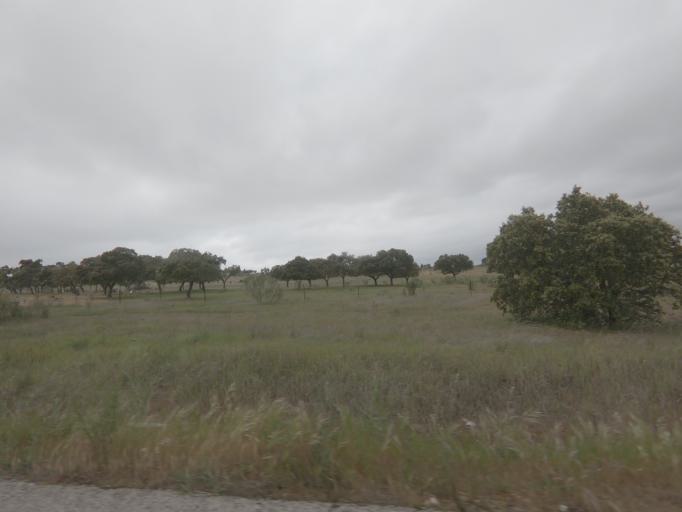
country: ES
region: Extremadura
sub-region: Provincia de Caceres
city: Malpartida de Caceres
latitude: 39.3653
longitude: -6.4601
